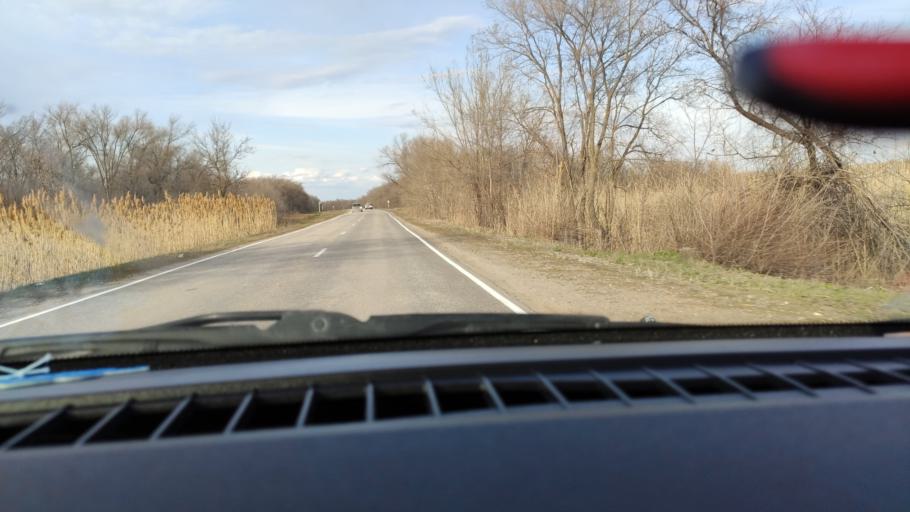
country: RU
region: Saratov
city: Privolzhskiy
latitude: 51.2428
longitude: 45.9322
